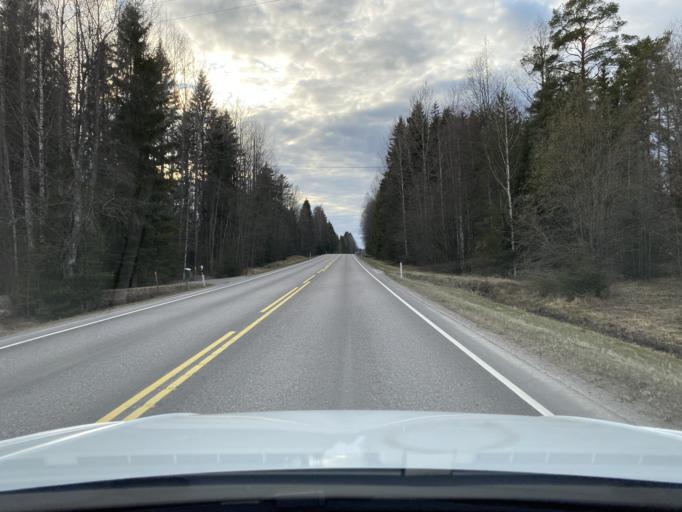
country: FI
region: Haeme
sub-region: Haemeenlinna
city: Renko
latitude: 60.7910
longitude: 24.1199
